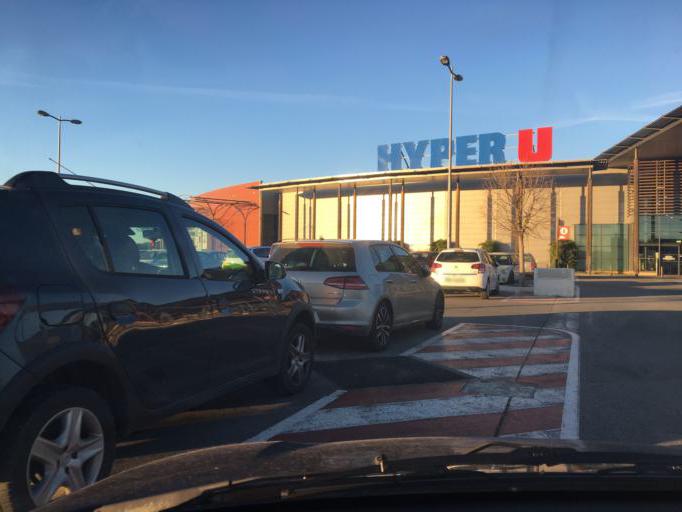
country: FR
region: Provence-Alpes-Cote d'Azur
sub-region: Departement du Var
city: Les Arcs
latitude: 43.4514
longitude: 6.4913
